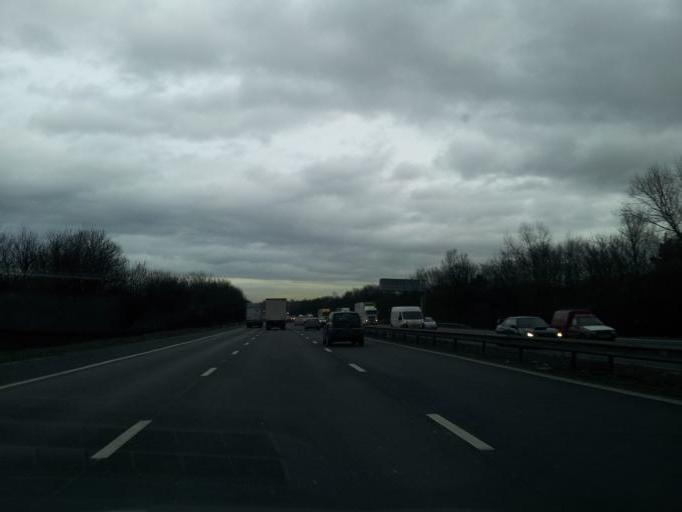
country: GB
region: England
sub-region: Solihull
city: Meriden
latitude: 52.4674
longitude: -1.6083
